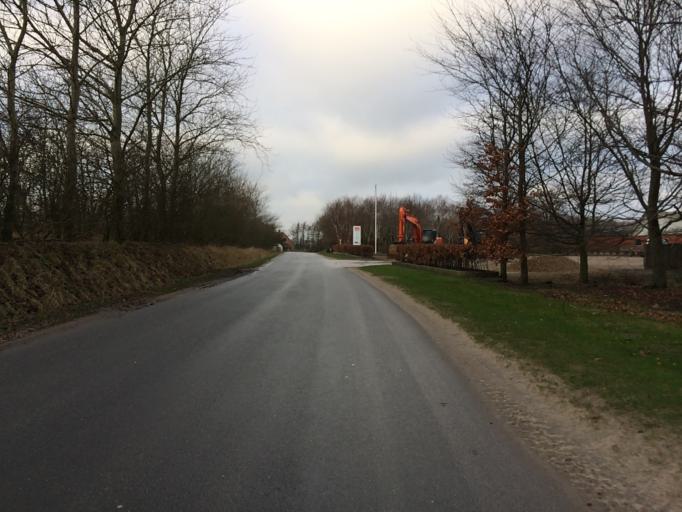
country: DK
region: Central Jutland
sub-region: Holstebro Kommune
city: Ulfborg
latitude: 56.2743
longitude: 8.2721
